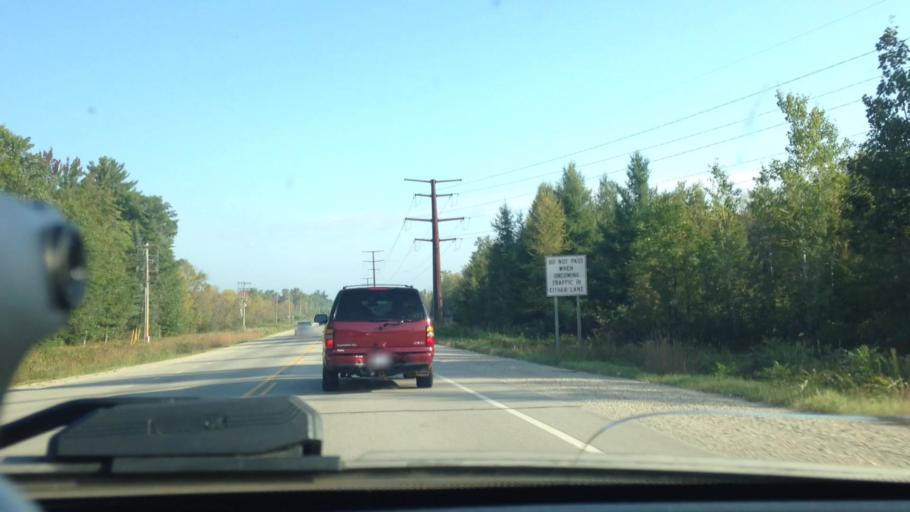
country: US
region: Wisconsin
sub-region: Marinette County
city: Peshtigo
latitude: 45.1772
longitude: -87.9958
